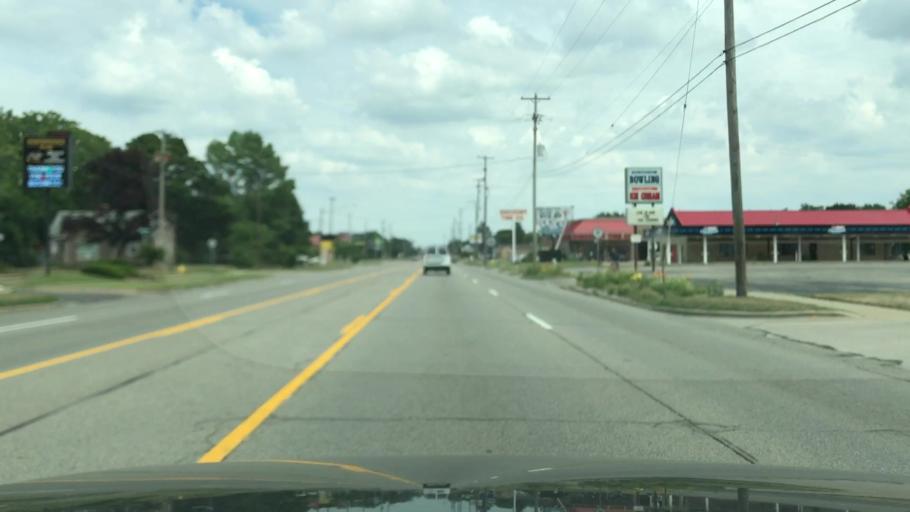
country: US
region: Michigan
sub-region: Kent County
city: Wyoming
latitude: 42.9138
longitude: -85.7208
